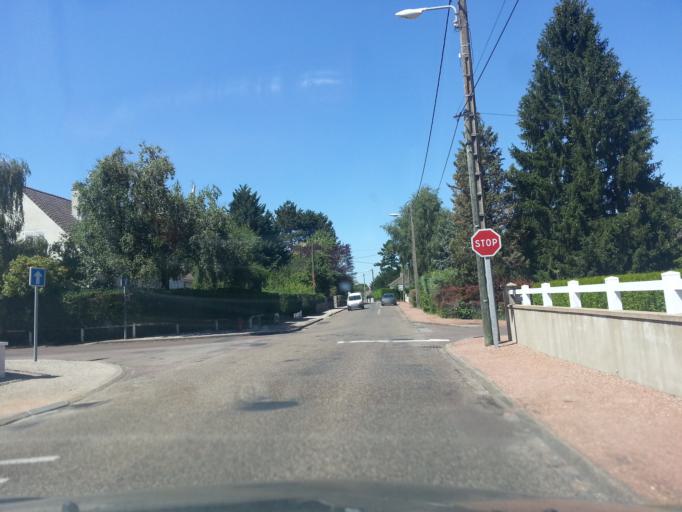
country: FR
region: Bourgogne
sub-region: Departement de Saone-et-Loire
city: Chatenoy-le-Royal
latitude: 46.7886
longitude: 4.8126
